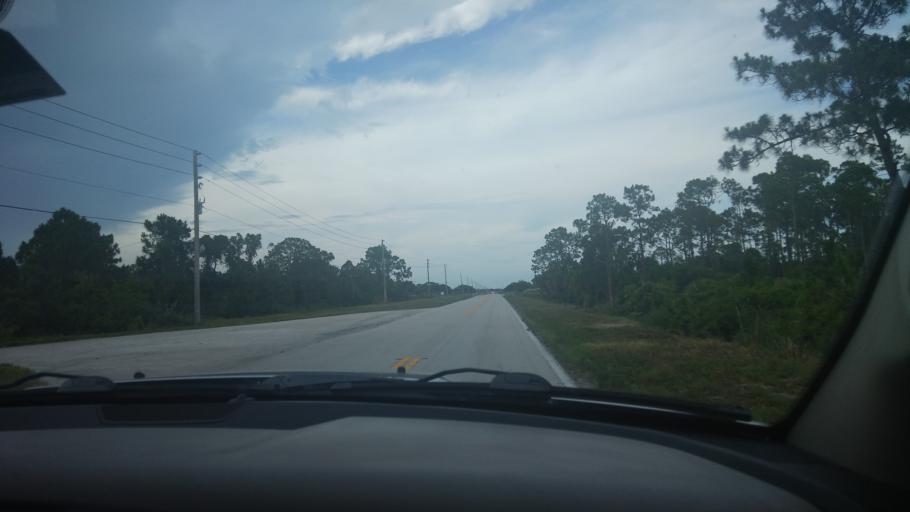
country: US
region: Florida
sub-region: Brevard County
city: Grant-Valkaria
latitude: 27.8865
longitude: -80.6225
